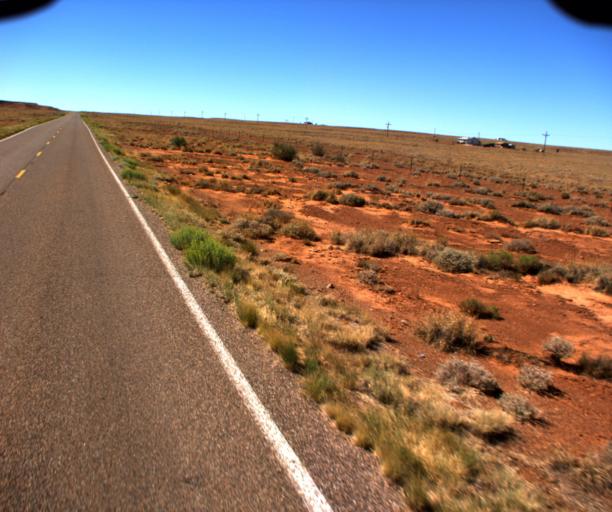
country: US
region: Arizona
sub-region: Coconino County
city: LeChee
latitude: 35.2121
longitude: -110.9503
